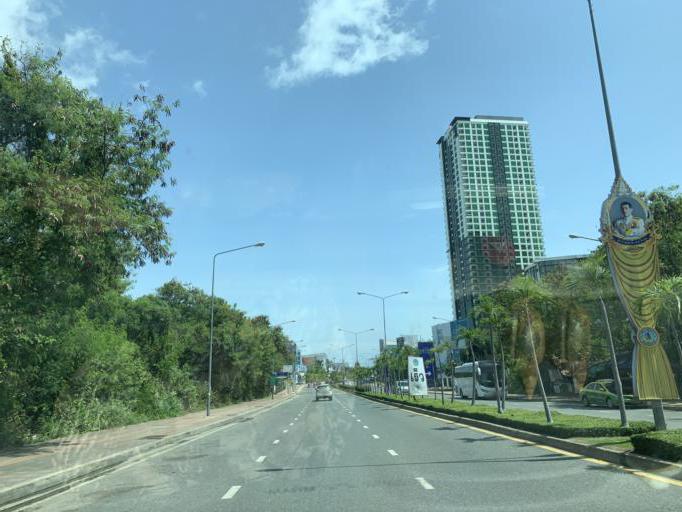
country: TH
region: Chon Buri
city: Phatthaya
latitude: 12.8917
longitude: 100.8785
